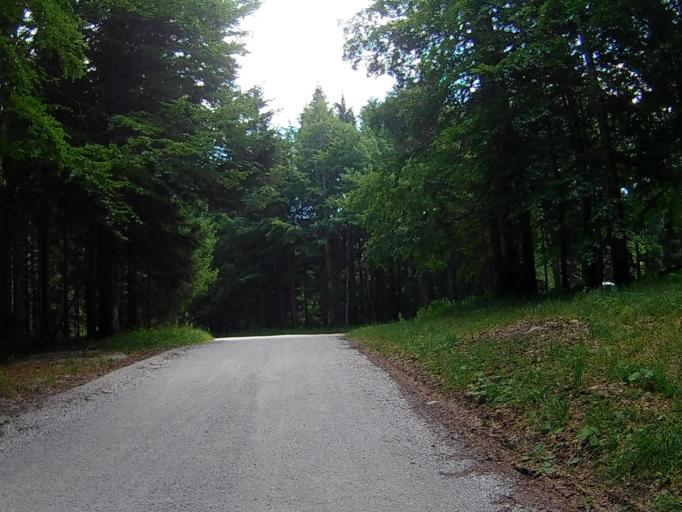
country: SI
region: Ruse
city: Ruse
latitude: 46.4979
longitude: 15.4976
